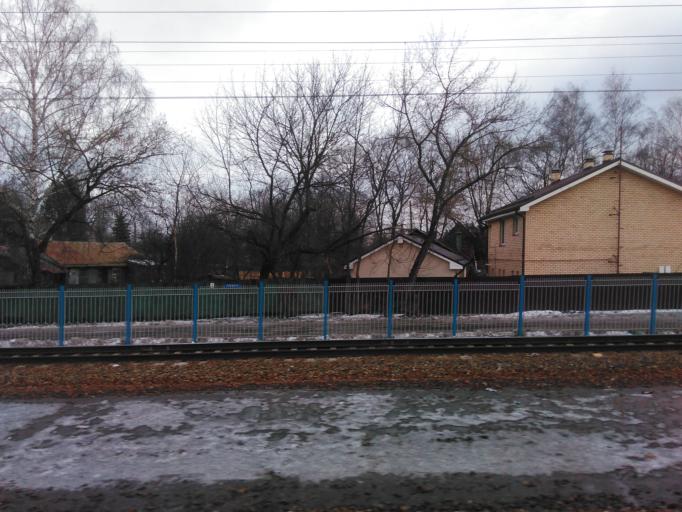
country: RU
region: Moskovskaya
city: Mamontovka
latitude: 55.9638
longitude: 37.8098
